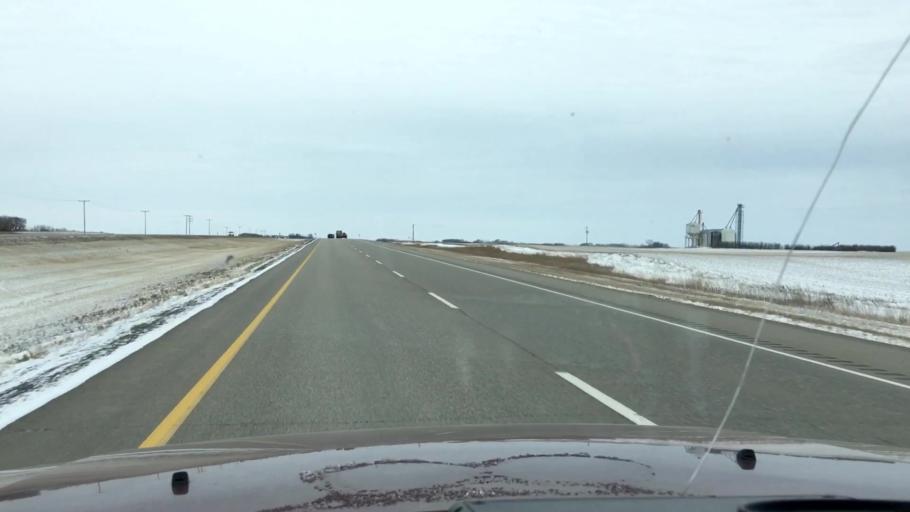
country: CA
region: Saskatchewan
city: Watrous
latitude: 51.2165
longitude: -105.9617
